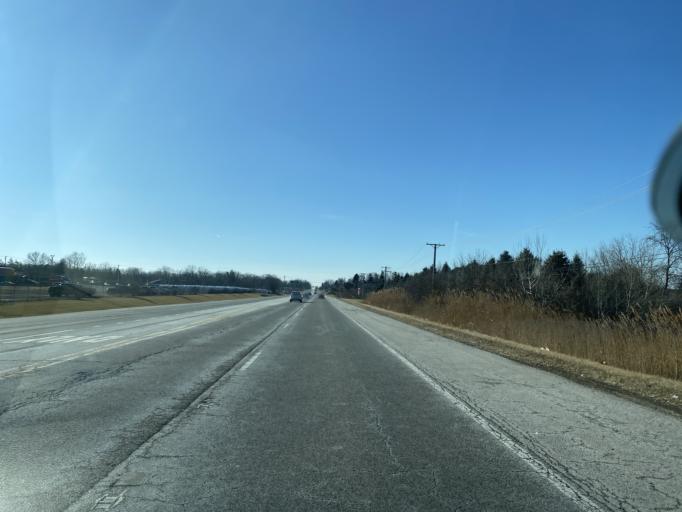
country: US
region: Illinois
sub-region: Cook County
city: Lemont
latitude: 41.6298
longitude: -88.0184
